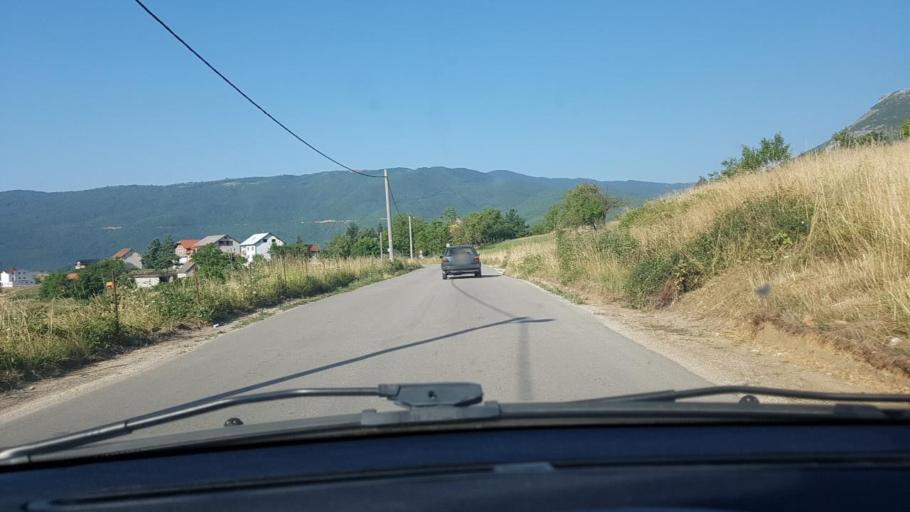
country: BA
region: Federation of Bosnia and Herzegovina
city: Rumboci
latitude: 43.8282
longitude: 17.5191
